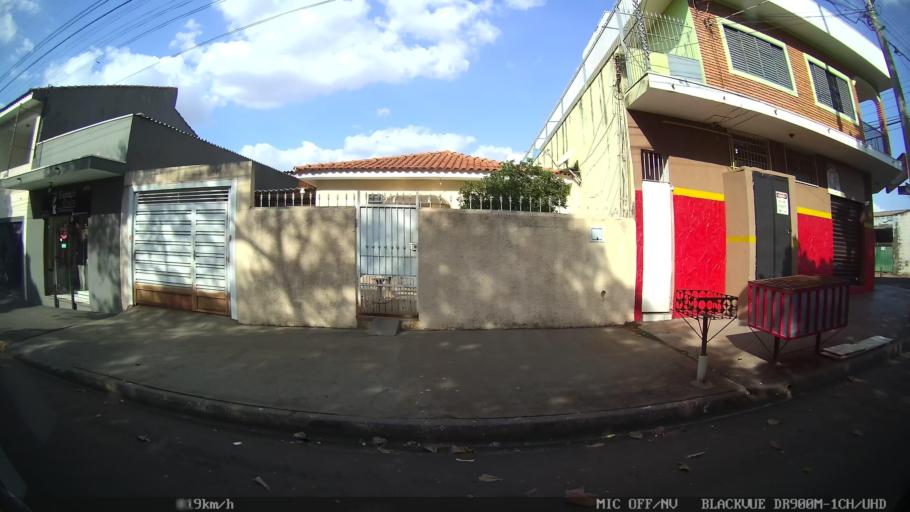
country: BR
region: Sao Paulo
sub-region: Ribeirao Preto
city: Ribeirao Preto
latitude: -21.1820
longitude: -47.8323
